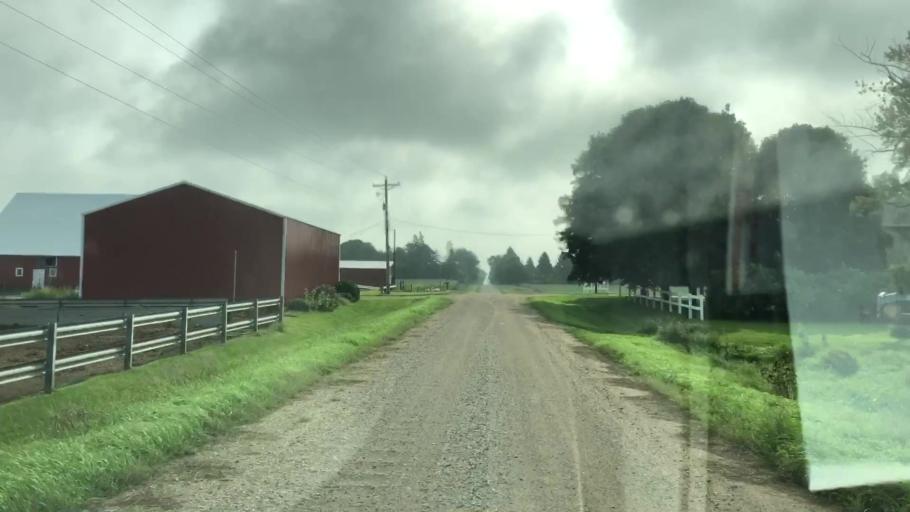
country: US
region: Iowa
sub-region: Lyon County
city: George
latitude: 43.2297
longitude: -96.0200
